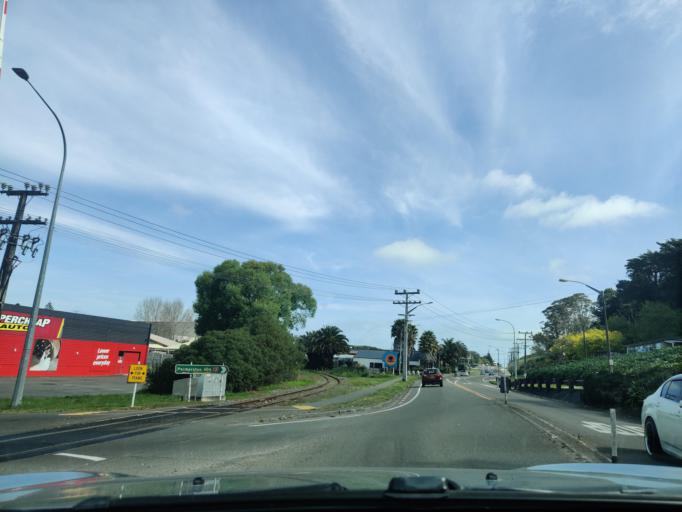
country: NZ
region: Manawatu-Wanganui
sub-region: Wanganui District
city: Wanganui
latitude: -39.9241
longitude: 175.0373
